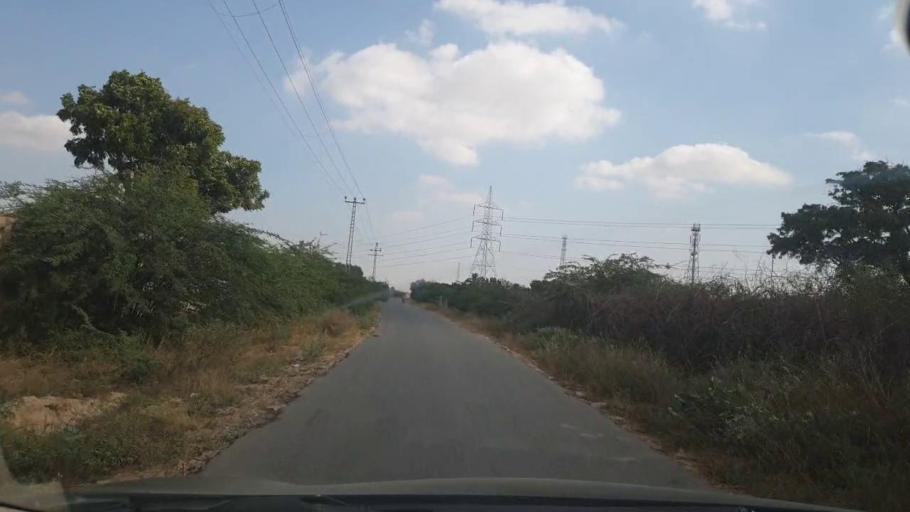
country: PK
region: Sindh
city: Malir Cantonment
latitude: 25.0194
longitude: 67.3639
